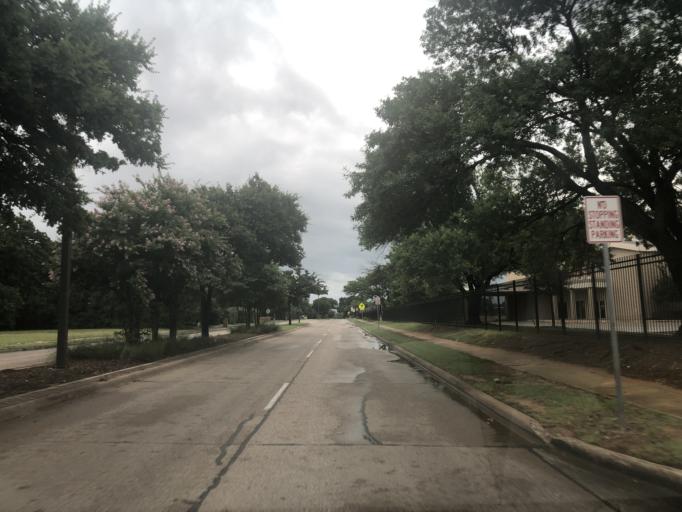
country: US
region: Texas
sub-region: Dallas County
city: Irving
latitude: 32.8004
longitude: -96.9592
